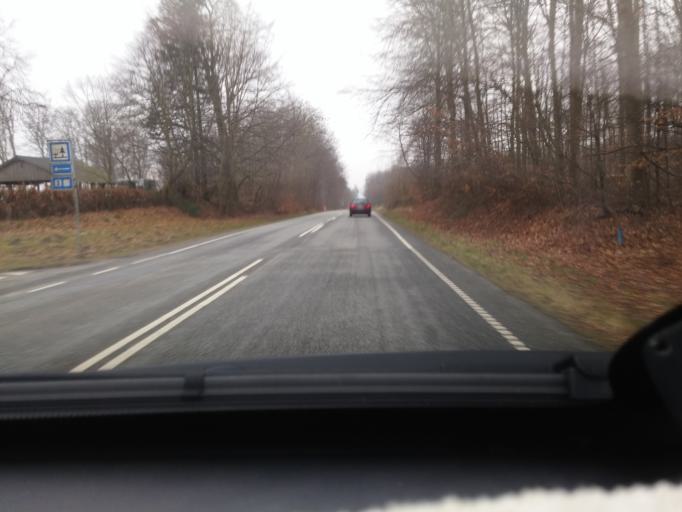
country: DK
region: South Denmark
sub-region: Kerteminde Kommune
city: Kerteminde
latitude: 55.4366
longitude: 10.6862
